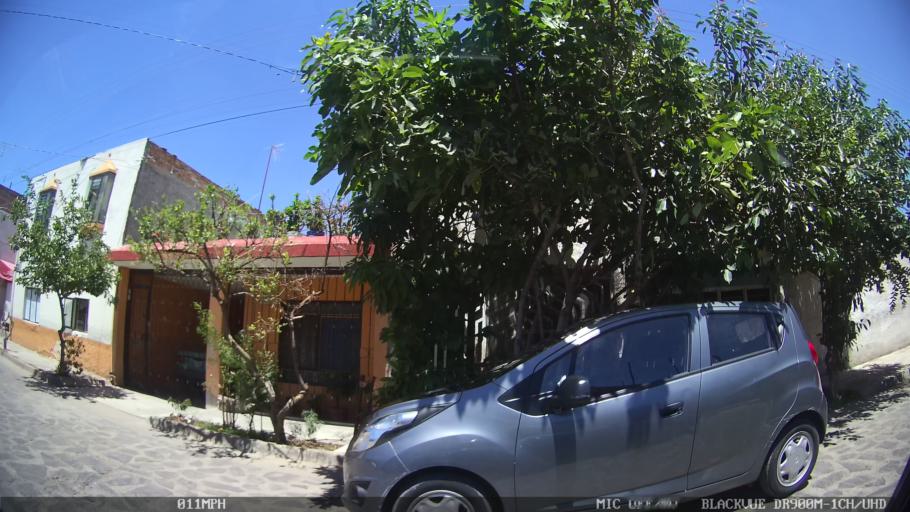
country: MX
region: Jalisco
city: Tlaquepaque
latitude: 20.6567
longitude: -103.2775
